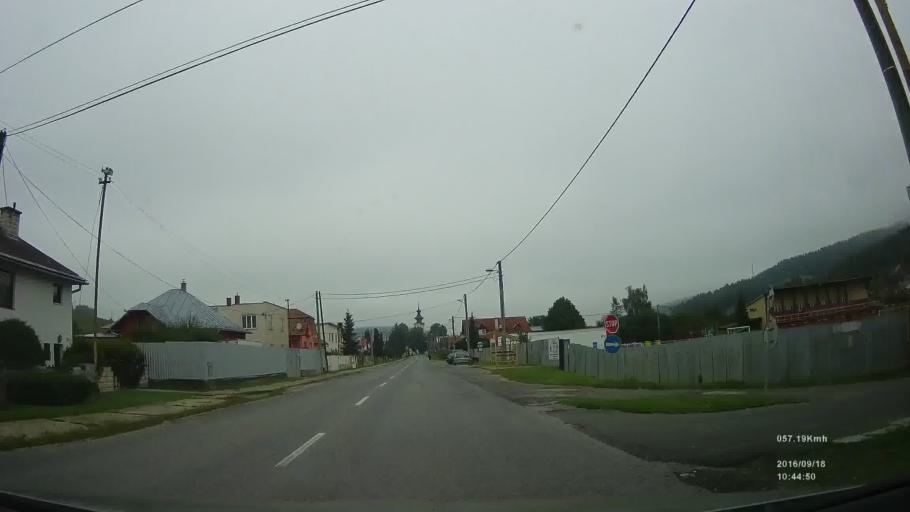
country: SK
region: Kosicky
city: Spisska Nova Ves
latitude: 48.9582
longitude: 20.5831
